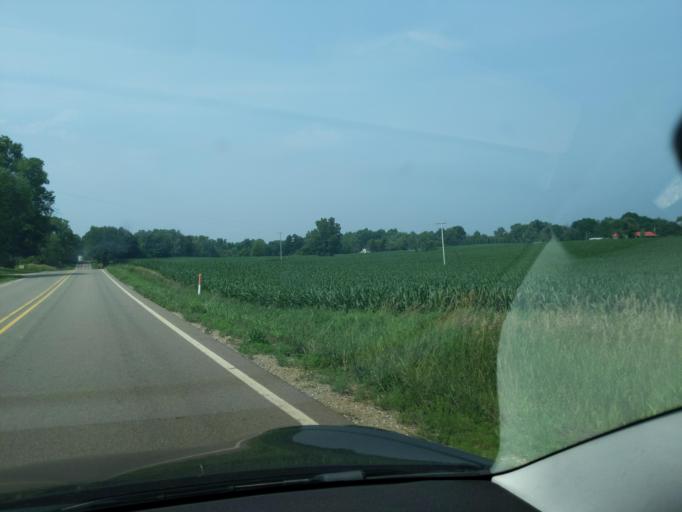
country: US
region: Michigan
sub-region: Clinton County
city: DeWitt
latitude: 42.8892
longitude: -84.5723
